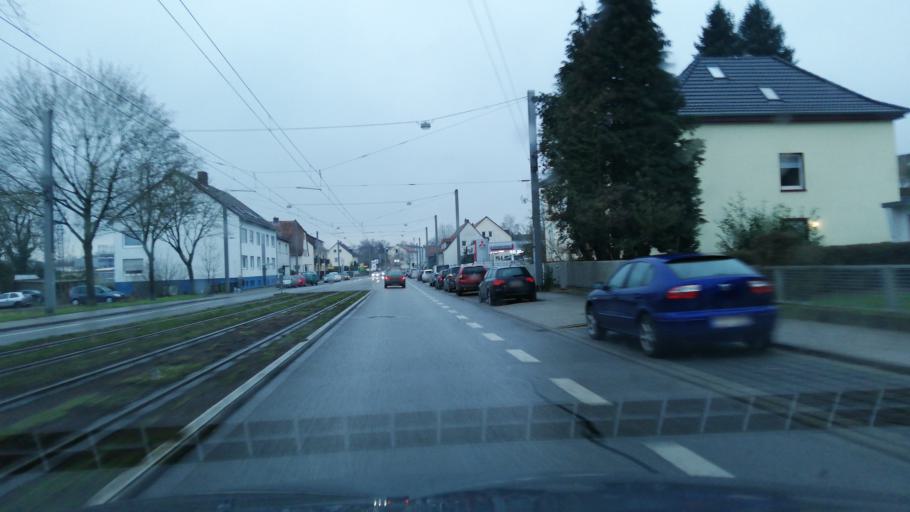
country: DE
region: Hesse
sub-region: Regierungsbezirk Kassel
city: Kassel
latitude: 51.3277
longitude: 9.5214
